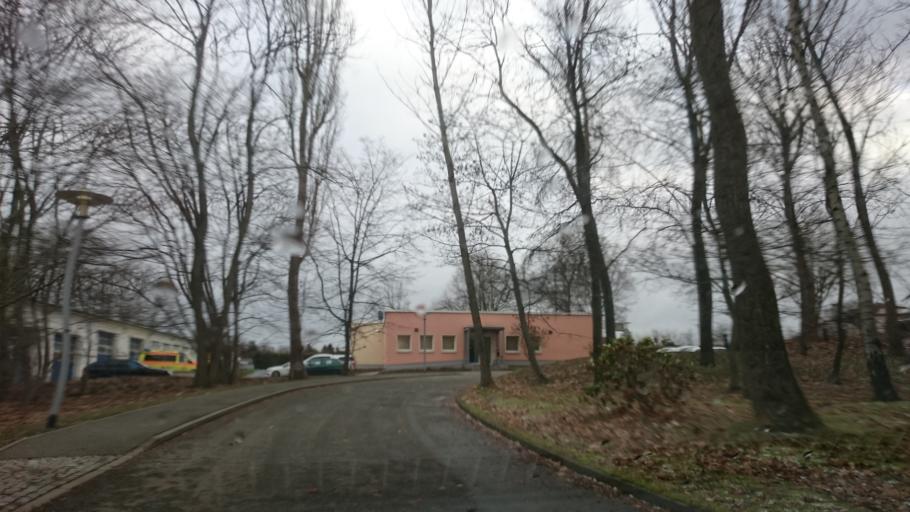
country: DE
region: Saxony
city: Werdau
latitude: 50.7373
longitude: 12.3869
